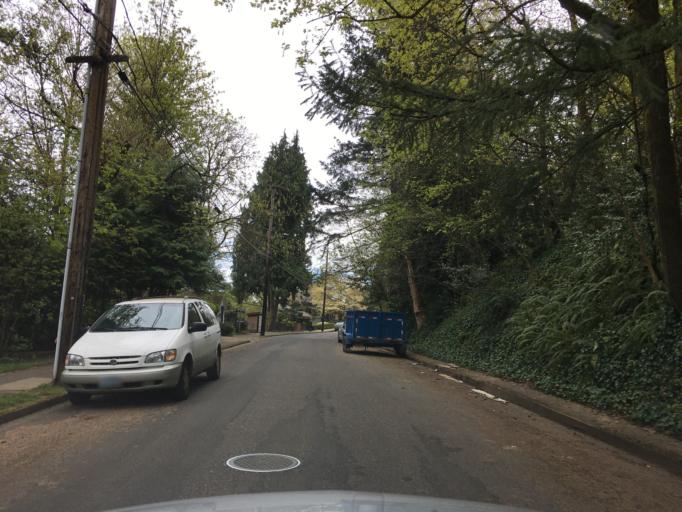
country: US
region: Oregon
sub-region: Multnomah County
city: Lents
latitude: 45.5210
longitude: -122.5909
